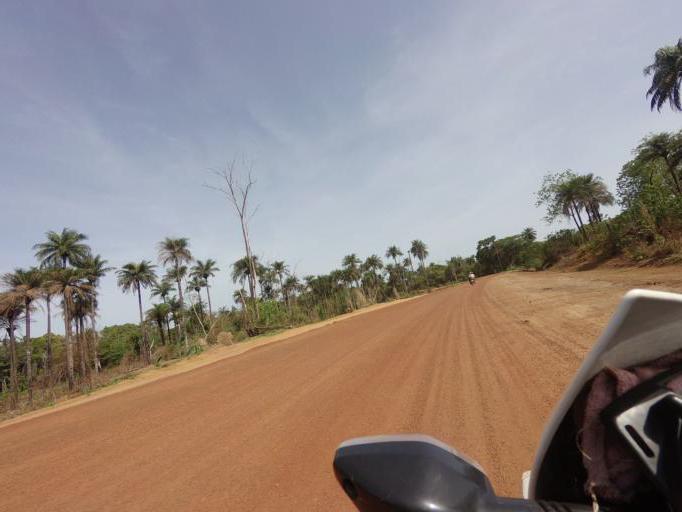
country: SL
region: Northern Province
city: Makeni
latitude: 9.0774
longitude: -12.1824
